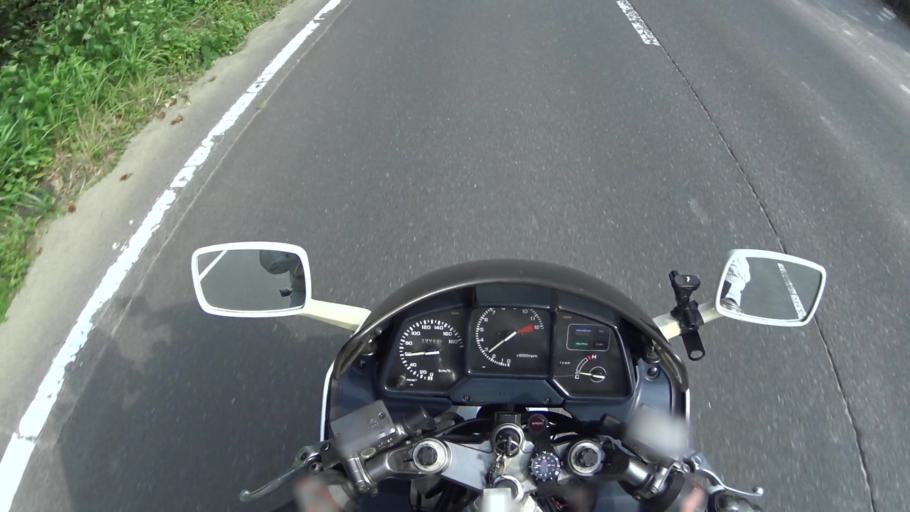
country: JP
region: Kyoto
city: Miyazu
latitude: 35.5752
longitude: 135.1042
